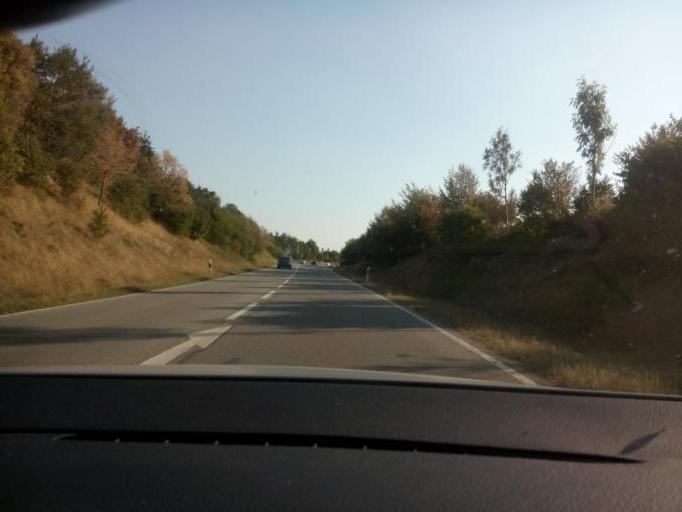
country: DE
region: Bavaria
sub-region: Upper Bavaria
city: Neubiberg
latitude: 48.0664
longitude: 11.6492
